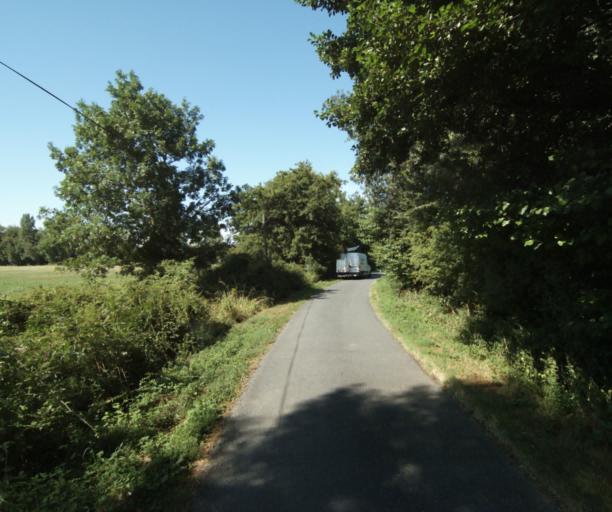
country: FR
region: Midi-Pyrenees
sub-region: Departement de la Haute-Garonne
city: Revel
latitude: 43.4791
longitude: 1.9912
